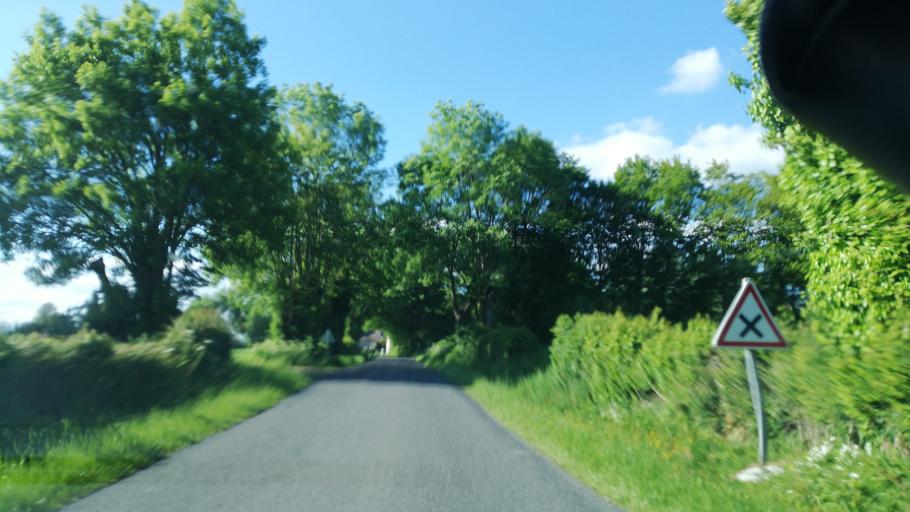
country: FR
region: Poitou-Charentes
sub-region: Departement des Deux-Sevres
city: Moncoutant
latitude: 46.6799
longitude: -0.5725
